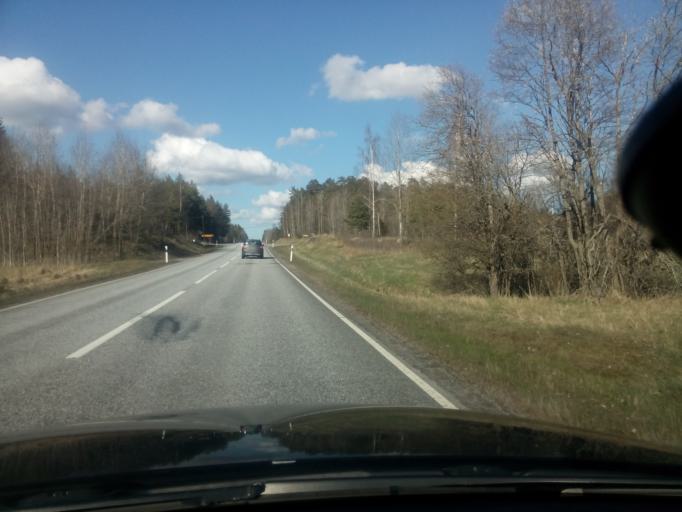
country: SE
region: Soedermanland
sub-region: Strangnas Kommun
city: Strangnas
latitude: 59.3118
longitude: 16.9961
